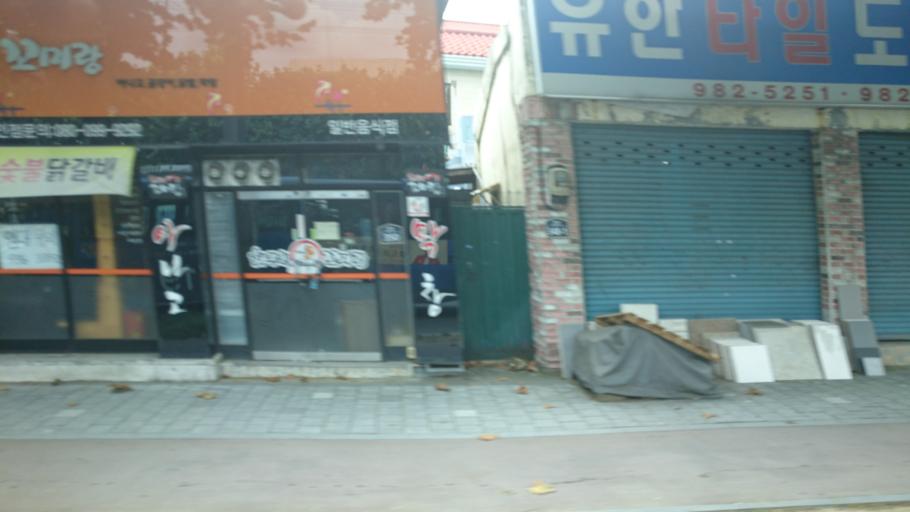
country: KR
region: Gyeongsangbuk-do
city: Gyeongsan-si
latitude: 35.8774
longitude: 128.6772
